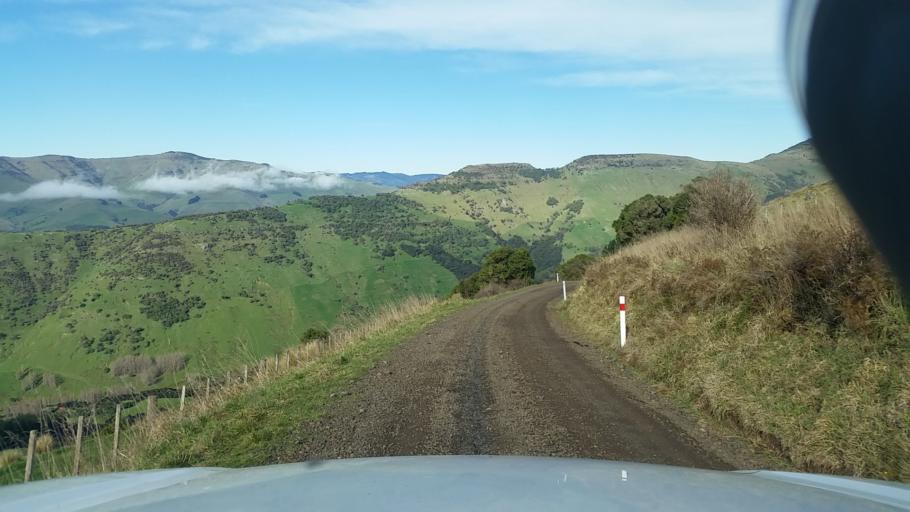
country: NZ
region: Canterbury
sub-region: Christchurch City
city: Christchurch
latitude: -43.6765
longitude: 172.8523
